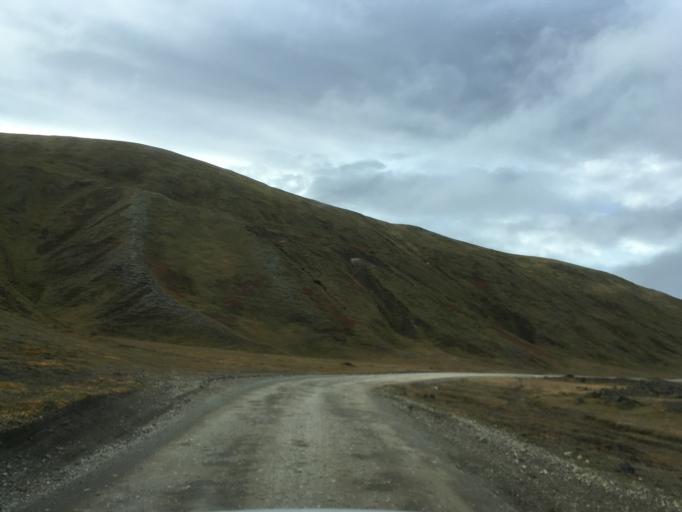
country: IS
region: South
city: Vestmannaeyjar
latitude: 64.0066
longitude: -19.0401
